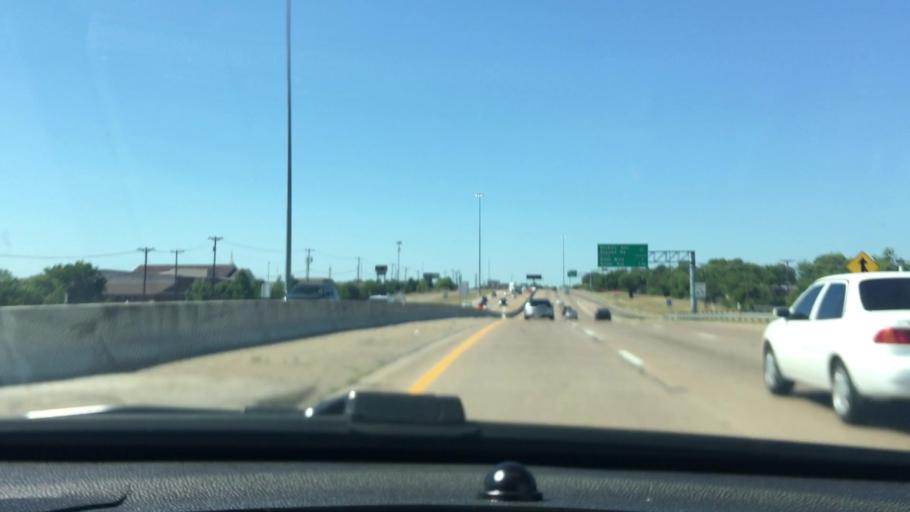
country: US
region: Texas
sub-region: Dallas County
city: Cockrell Hill
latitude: 32.6916
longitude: -96.8231
